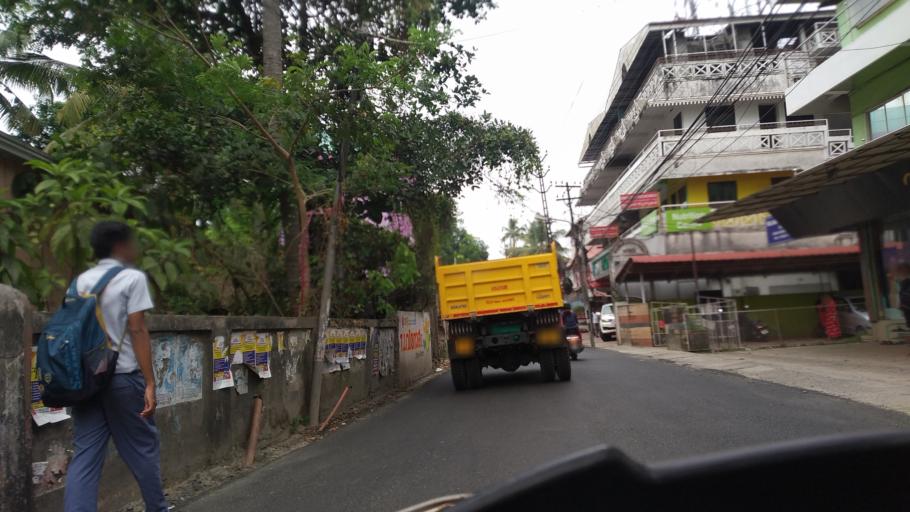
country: IN
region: Kerala
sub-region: Ernakulam
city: Cochin
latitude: 9.9366
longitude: 76.2973
